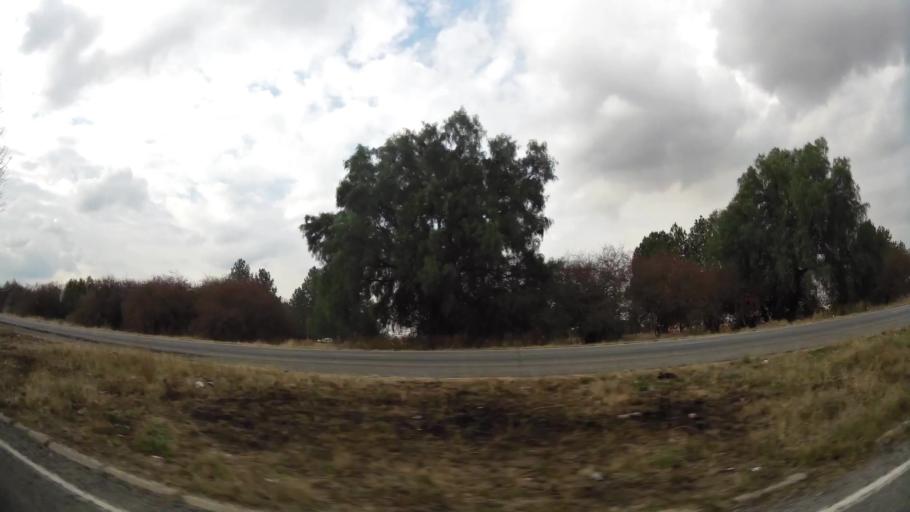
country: ZA
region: Orange Free State
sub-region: Fezile Dabi District Municipality
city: Sasolburg
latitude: -26.8034
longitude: 27.8341
